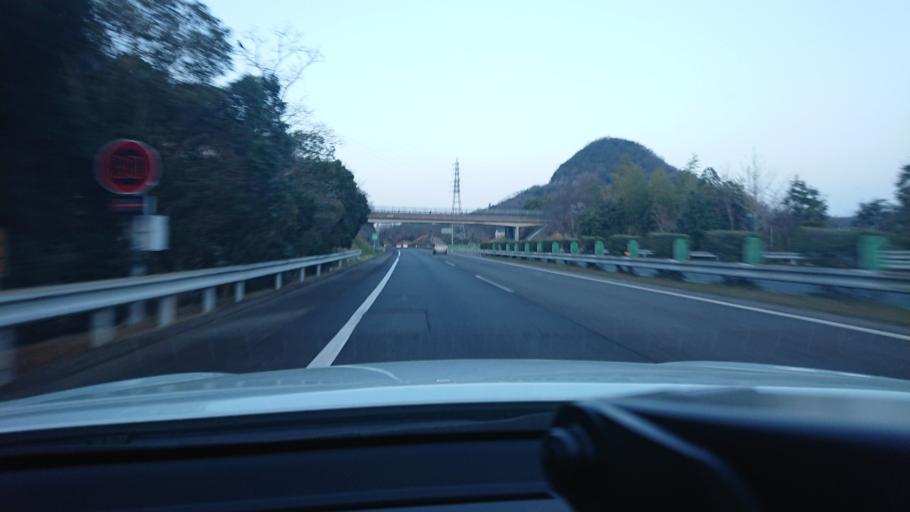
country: JP
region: Kagawa
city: Takamatsu-shi
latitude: 34.2955
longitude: 133.9830
